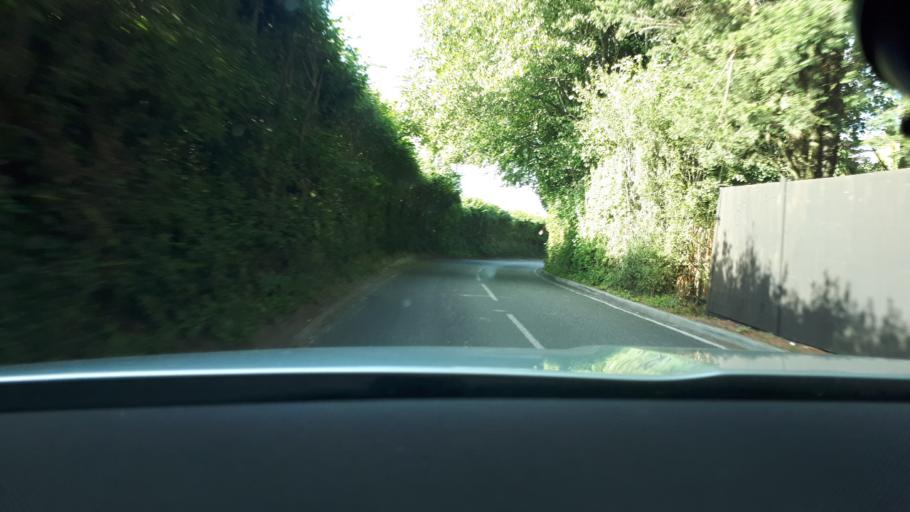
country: GB
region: England
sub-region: Greater London
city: Orpington
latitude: 51.3396
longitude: 0.0803
